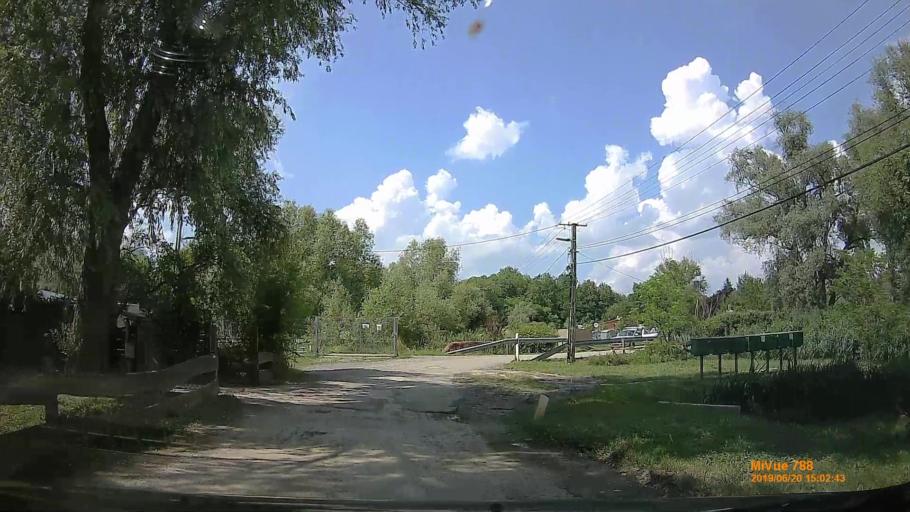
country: HU
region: Baranya
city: Kozarmisleny
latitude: 45.9853
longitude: 18.2627
